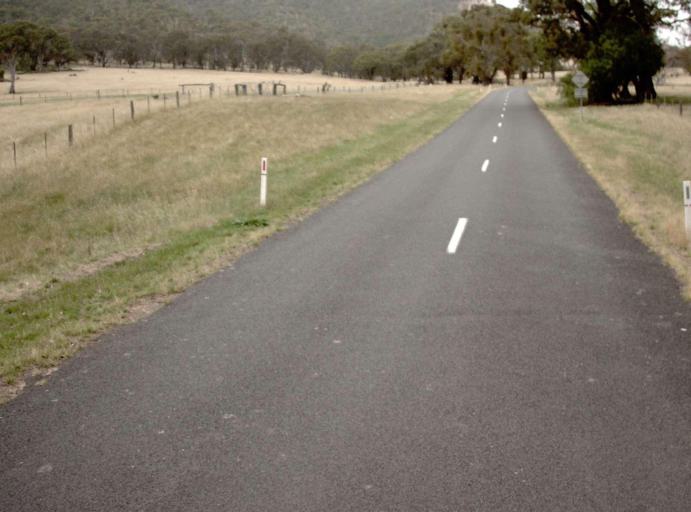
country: AU
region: Victoria
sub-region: Wellington
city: Heyfield
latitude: -37.6457
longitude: 146.6407
